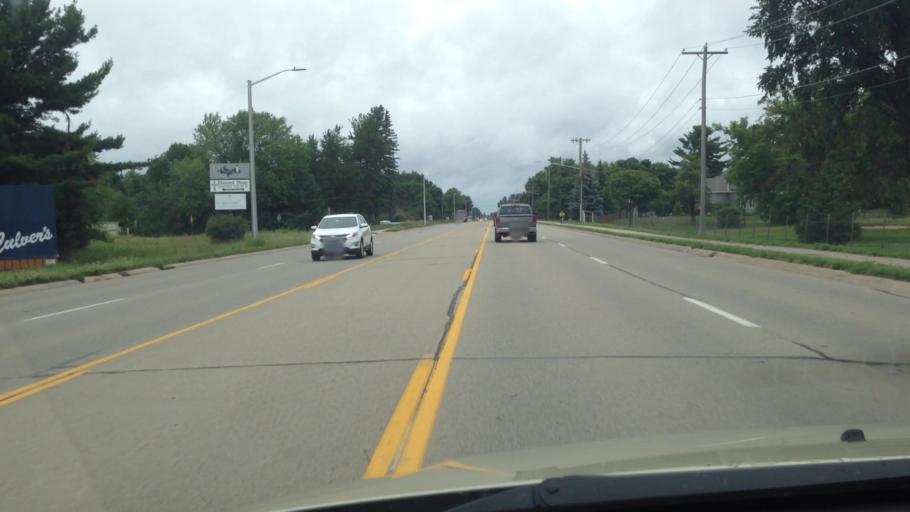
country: US
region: Michigan
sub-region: Delta County
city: Escanaba
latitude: 45.7290
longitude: -87.0800
